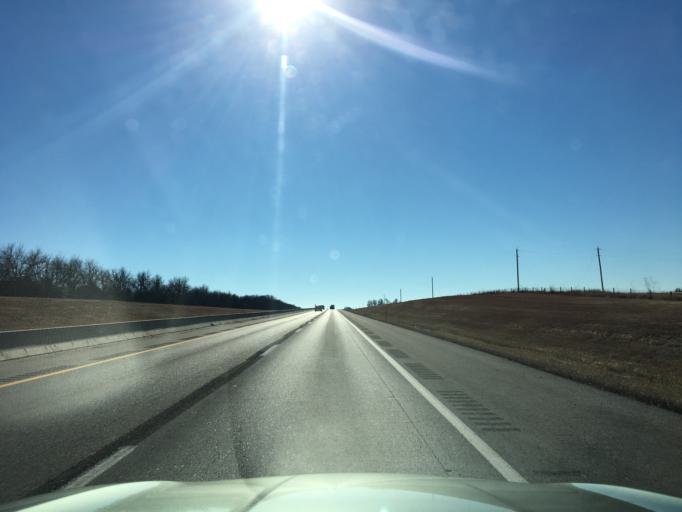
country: US
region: Kansas
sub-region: Sumner County
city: Wellington
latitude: 37.0856
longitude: -97.3387
